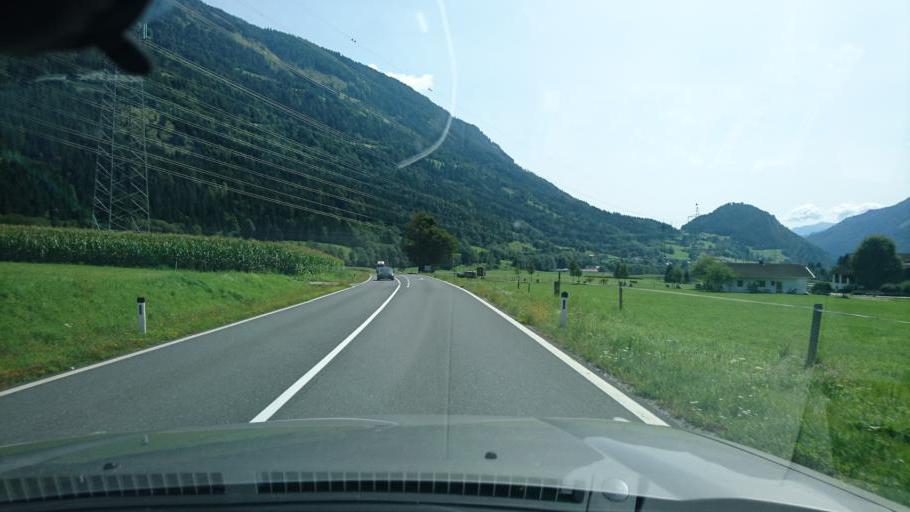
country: AT
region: Carinthia
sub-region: Politischer Bezirk Spittal an der Drau
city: Obervellach
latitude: 46.9074
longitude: 13.2474
